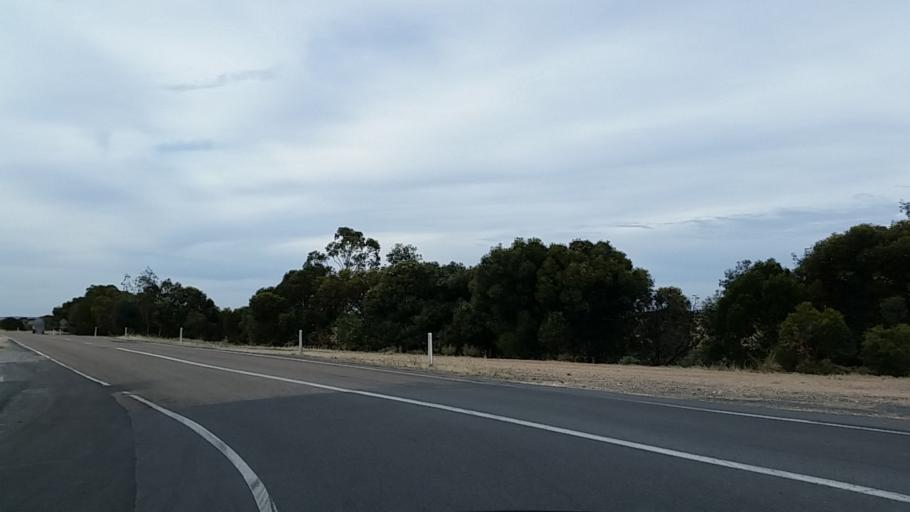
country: AU
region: South Australia
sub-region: Murray Bridge
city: Murray Bridge
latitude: -35.0351
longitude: 139.2065
